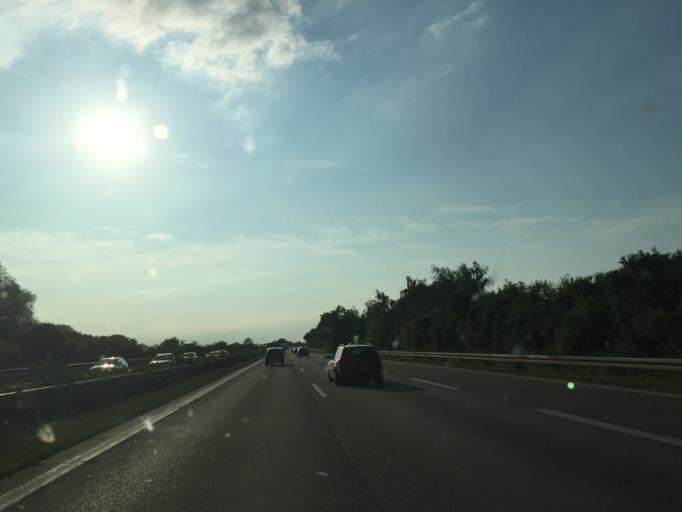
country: DE
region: Baden-Wuerttemberg
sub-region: Regierungsbezirk Stuttgart
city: Bad Rappenau
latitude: 49.1958
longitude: 9.1015
